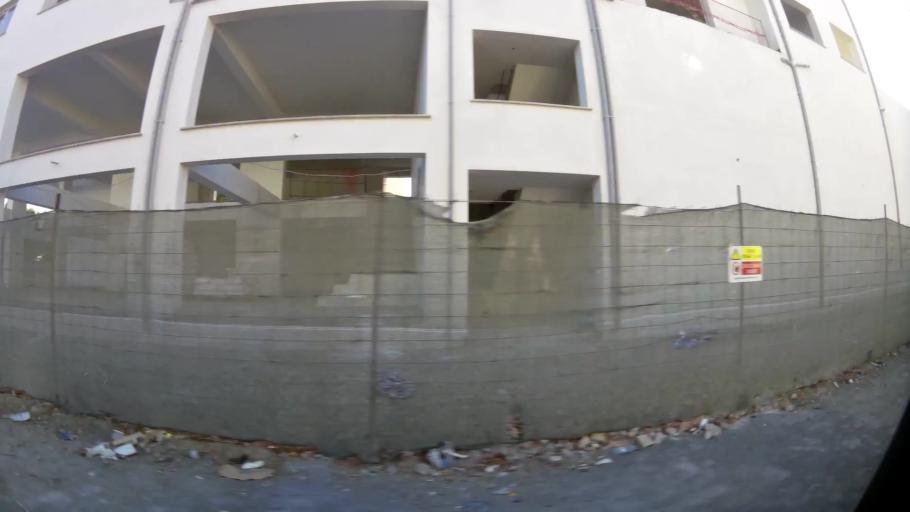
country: CY
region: Lefkosia
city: Nicosia
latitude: 35.1999
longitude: 33.3275
